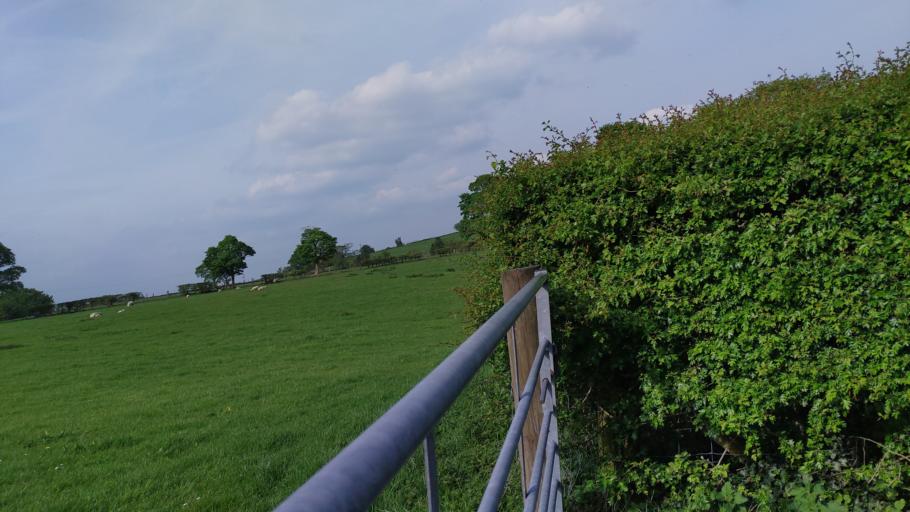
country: GB
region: England
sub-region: Lancashire
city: Chorley
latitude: 53.6870
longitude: -2.5981
